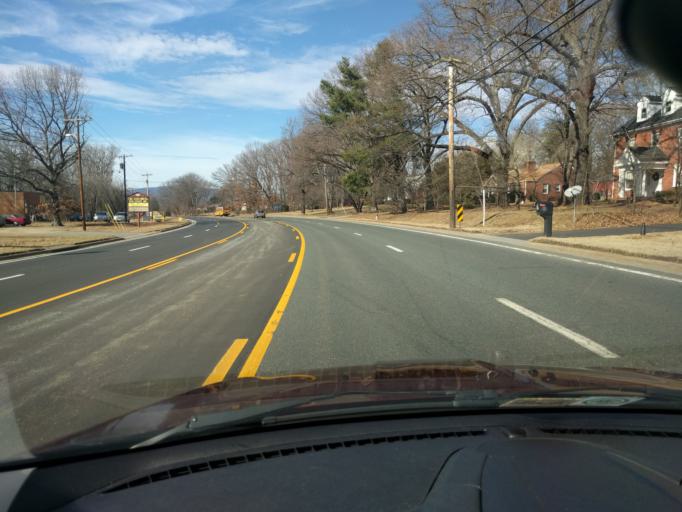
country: US
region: Virginia
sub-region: Amherst County
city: Madison Heights
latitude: 37.4842
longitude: -79.1192
